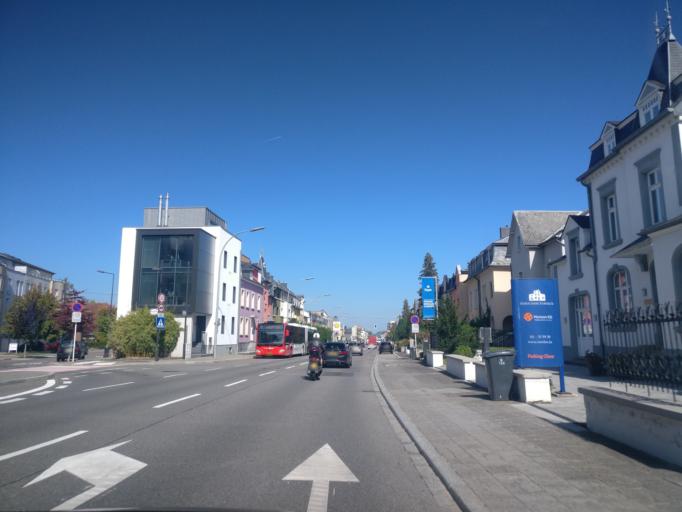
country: LU
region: Luxembourg
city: Bereldange
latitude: 49.6468
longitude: 6.1281
